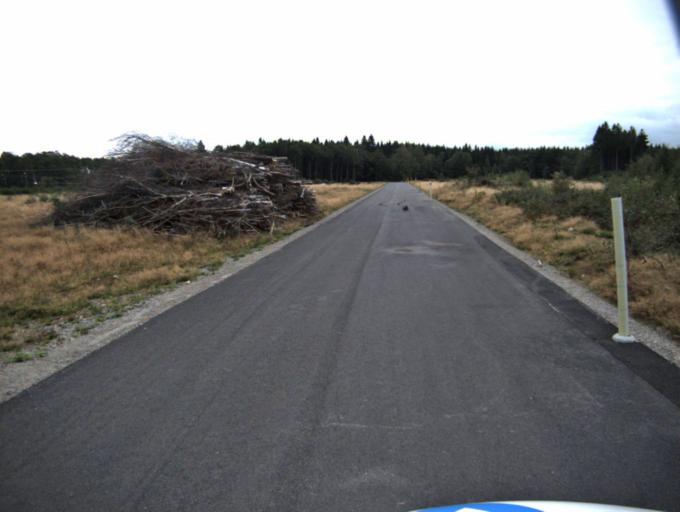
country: SE
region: Vaestra Goetaland
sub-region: Ulricehamns Kommun
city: Ulricehamn
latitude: 57.8034
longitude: 13.4480
